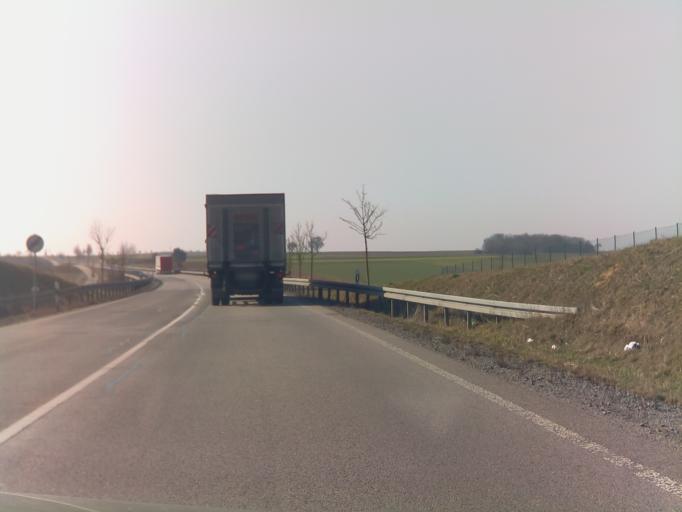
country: DE
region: Baden-Wuerttemberg
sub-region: Regierungsbezirk Stuttgart
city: Motzingen
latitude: 48.4982
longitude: 8.7903
